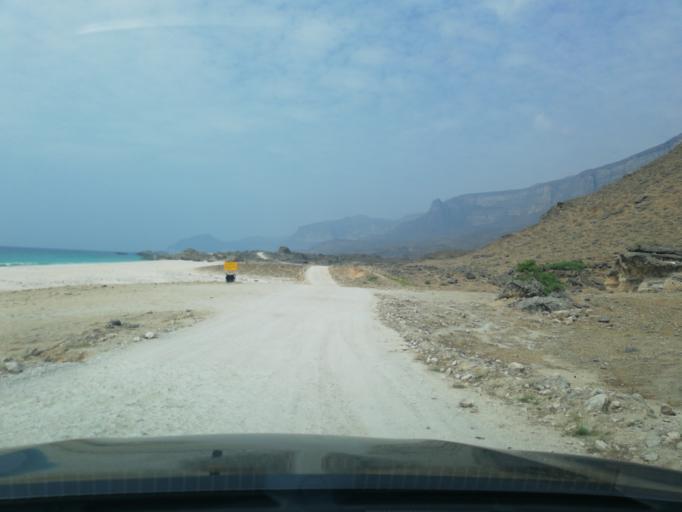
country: OM
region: Zufar
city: Salalah
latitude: 16.8409
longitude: 53.7219
